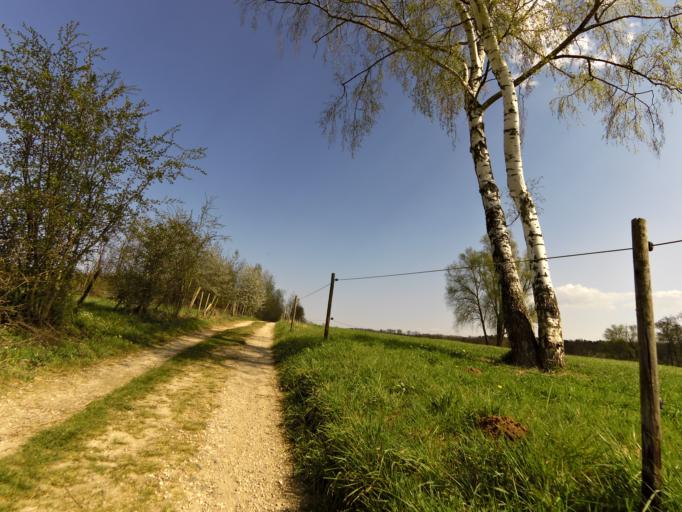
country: DE
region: North Rhine-Westphalia
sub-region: Regierungsbezirk Koln
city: Alfter
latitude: 50.6809
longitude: 7.0131
